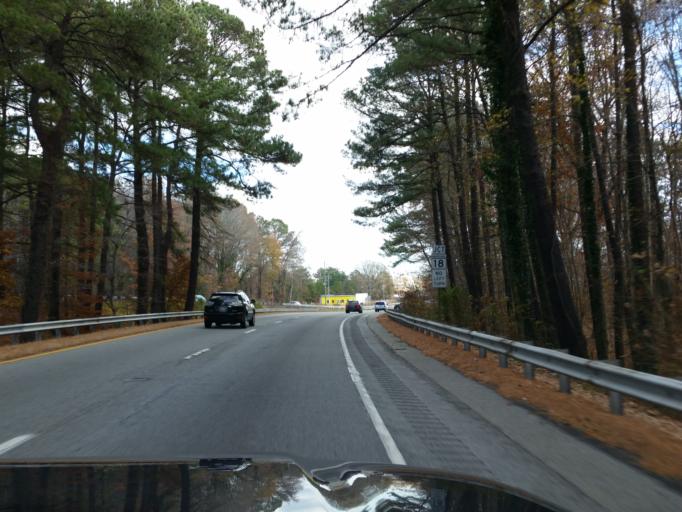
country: US
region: Maryland
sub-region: Queen Anne's County
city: Grasonville
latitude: 38.9809
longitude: -76.1677
